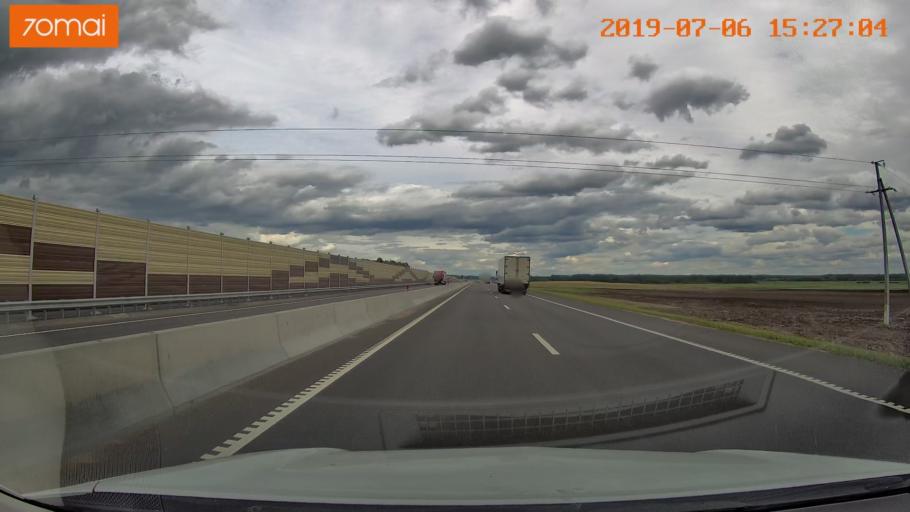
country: BY
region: Minsk
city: Valozhyn
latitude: 54.0377
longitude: 26.6345
